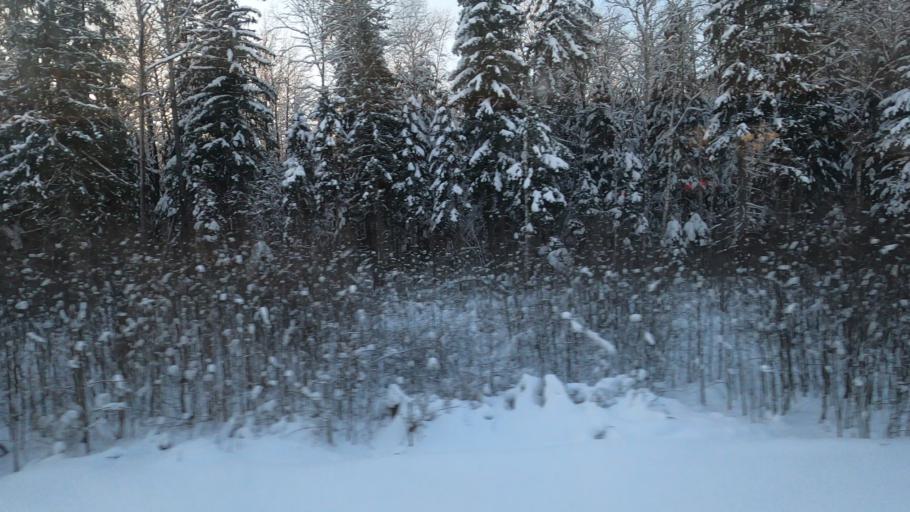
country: RU
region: Moskovskaya
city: Novo-Nikol'skoye
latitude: 56.6045
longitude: 37.5678
